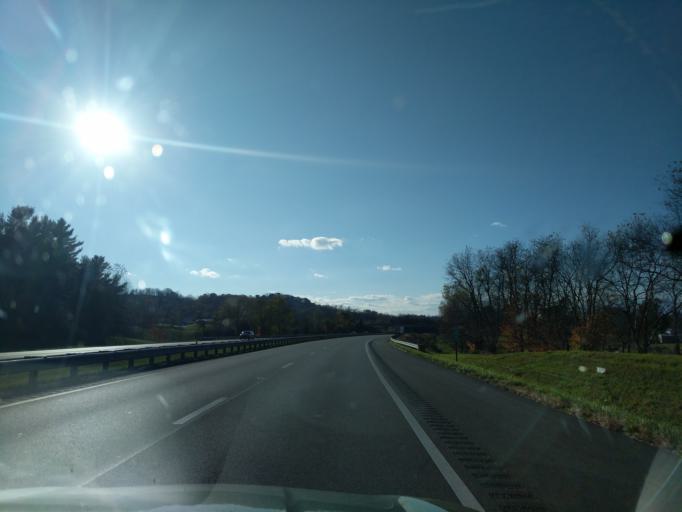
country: US
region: Virginia
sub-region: Smyth County
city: Adwolf
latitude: 36.8119
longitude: -81.5688
